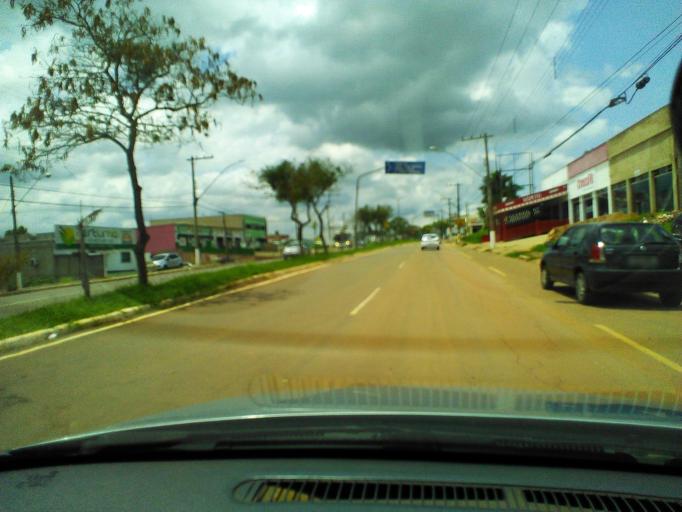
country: BR
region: Minas Gerais
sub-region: Tres Coracoes
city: Tres Coracoes
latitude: -21.6763
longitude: -45.2694
